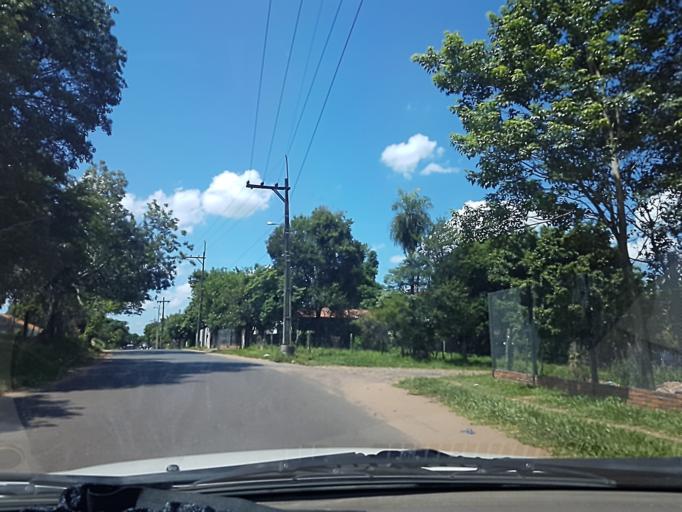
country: PY
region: Central
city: San Lorenzo
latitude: -25.2605
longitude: -57.4954
